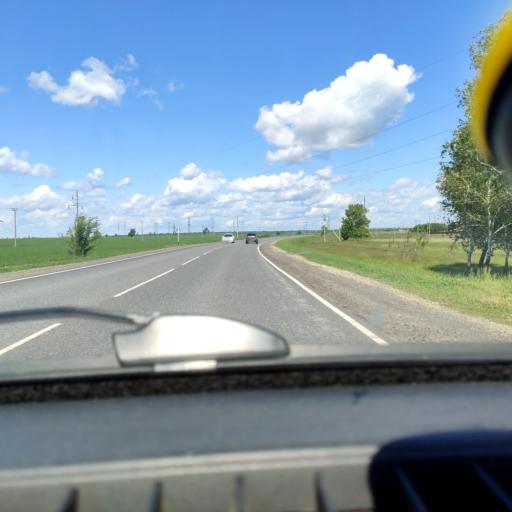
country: RU
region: Samara
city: Povolzhskiy
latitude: 53.6336
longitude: 49.6587
